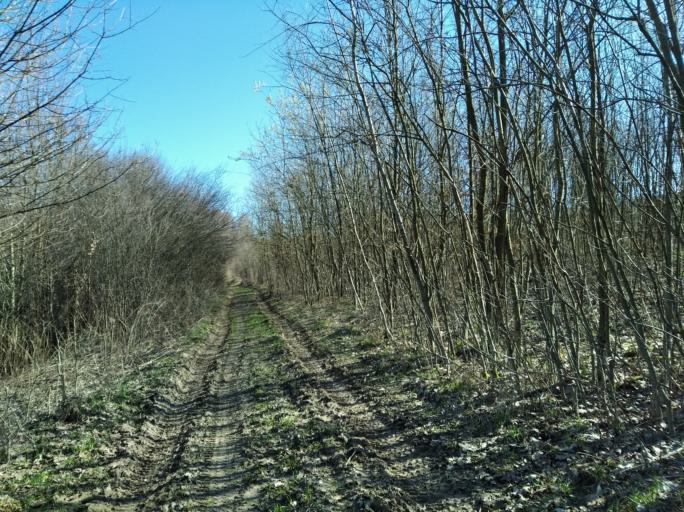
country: PL
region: Subcarpathian Voivodeship
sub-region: Powiat strzyzowski
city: Jawornik
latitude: 49.8314
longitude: 21.8479
